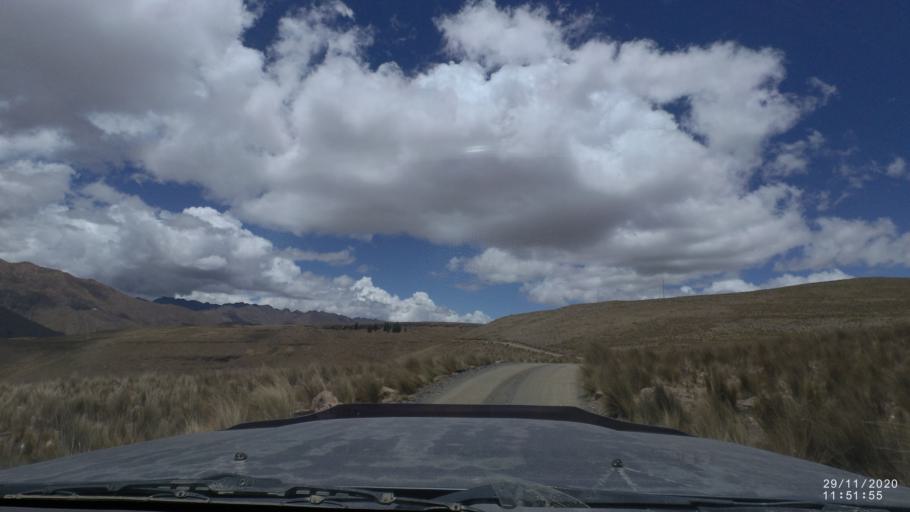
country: BO
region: Cochabamba
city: Cochabamba
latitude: -17.1722
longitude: -66.2643
